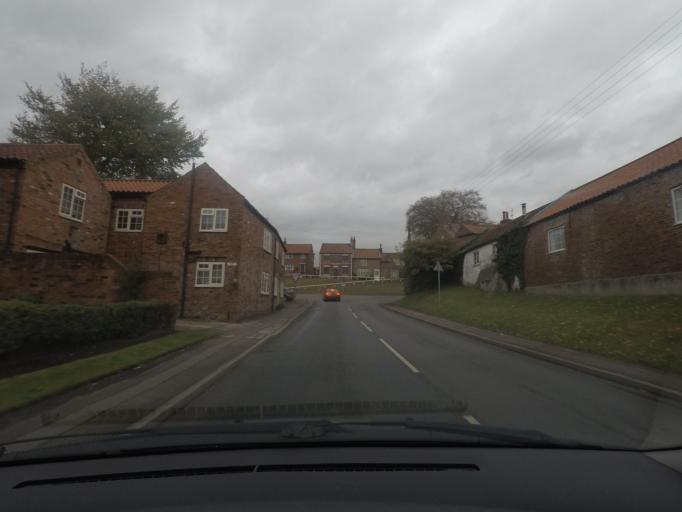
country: GB
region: England
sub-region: North Yorkshire
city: Easingwold
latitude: 54.1023
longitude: -1.1107
